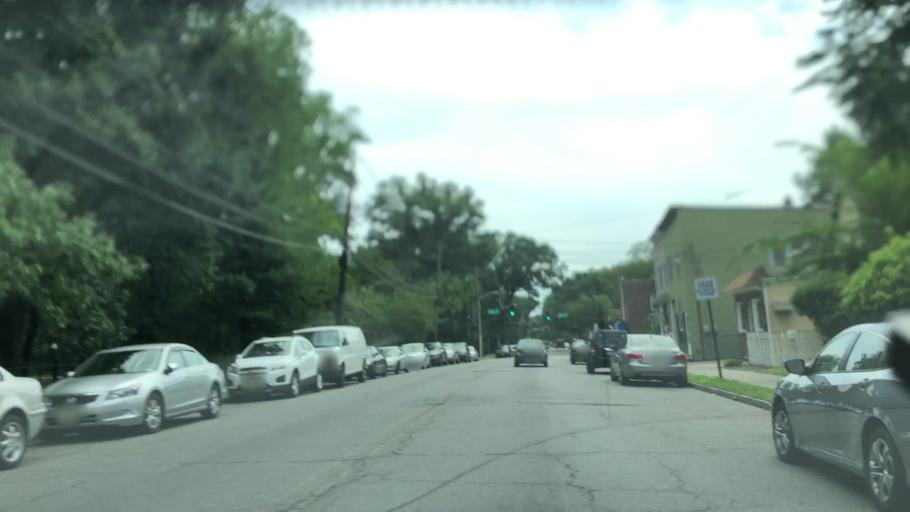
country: US
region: New Jersey
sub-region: Essex County
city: Glen Ridge
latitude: 40.7889
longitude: -74.2023
